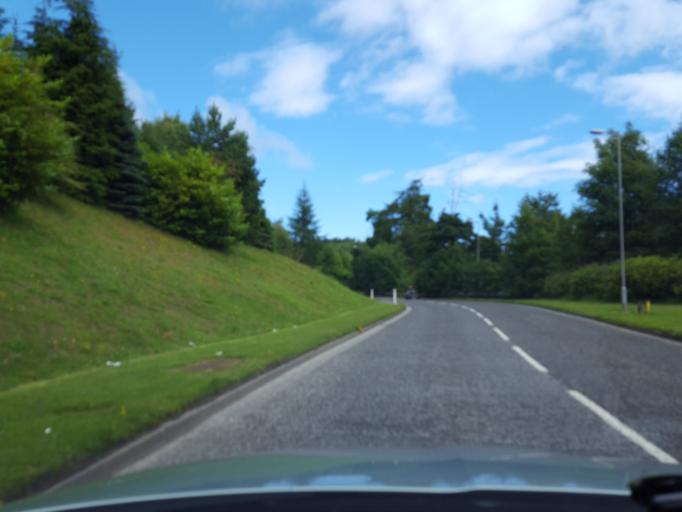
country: GB
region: Scotland
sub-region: Moray
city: Rothes
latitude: 57.5319
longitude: -3.2091
